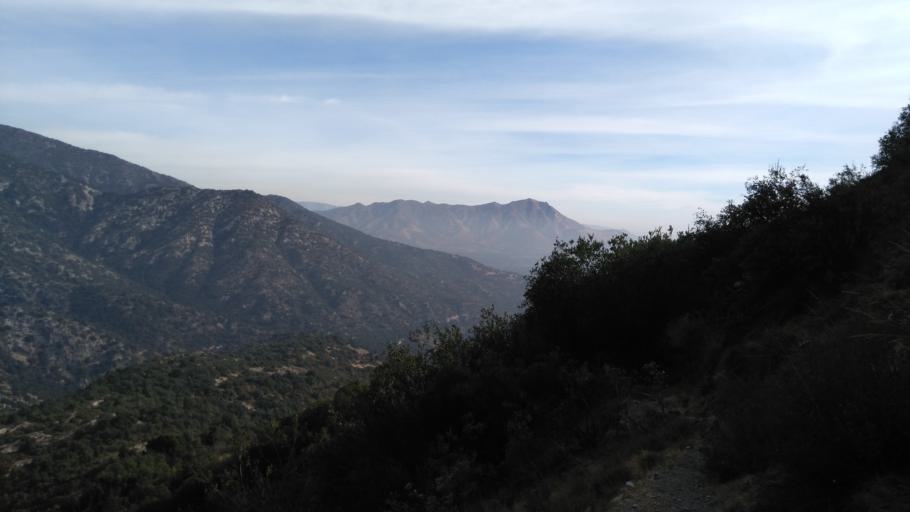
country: CL
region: Santiago Metropolitan
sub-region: Provincia de Cordillera
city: Puente Alto
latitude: -33.7224
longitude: -70.4548
